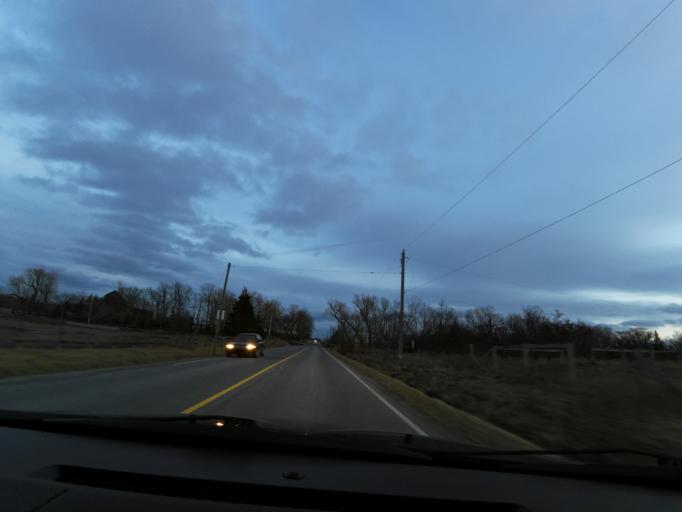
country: CA
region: Ontario
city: Burlington
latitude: 43.4123
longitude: -79.8509
